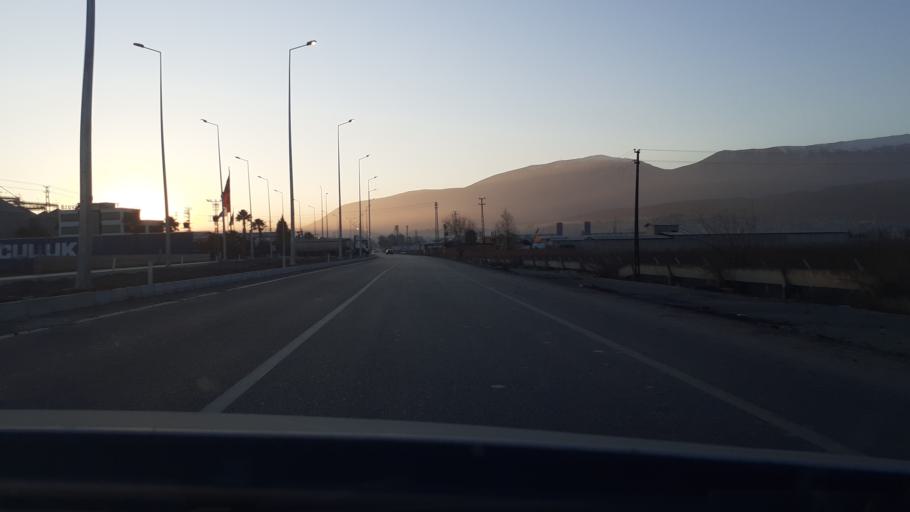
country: TR
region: Hatay
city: Kirikhan
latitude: 36.5022
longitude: 36.3911
